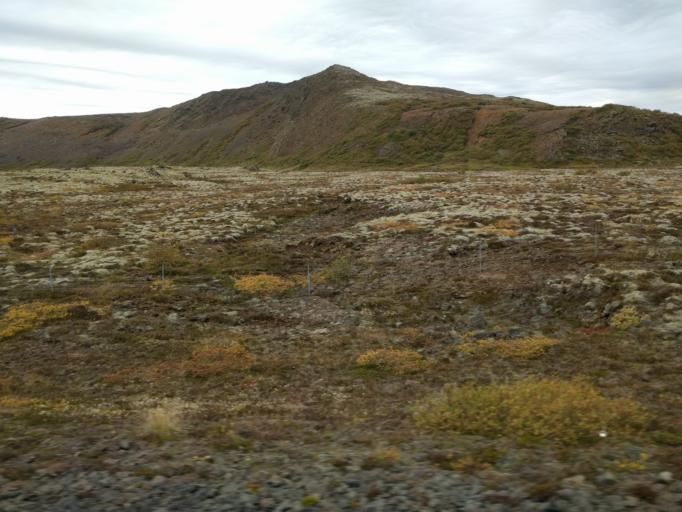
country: IS
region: South
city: Hveragerdi
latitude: 64.2237
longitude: -21.0538
